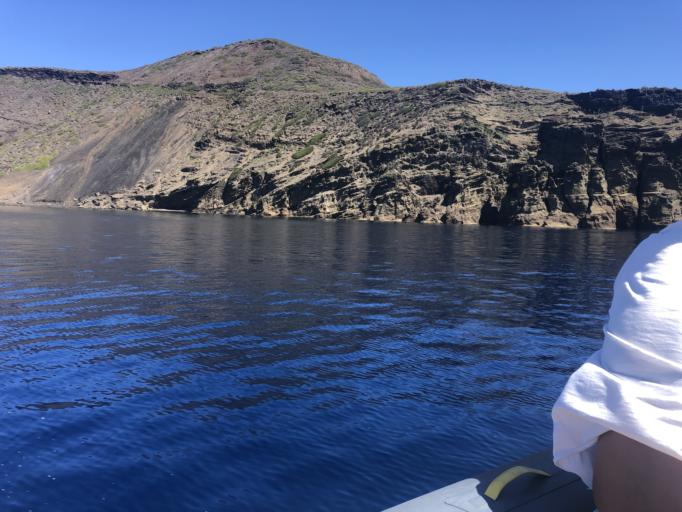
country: IT
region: Sicily
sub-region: Agrigento
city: Lampedusa
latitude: 35.8537
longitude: 12.8742
